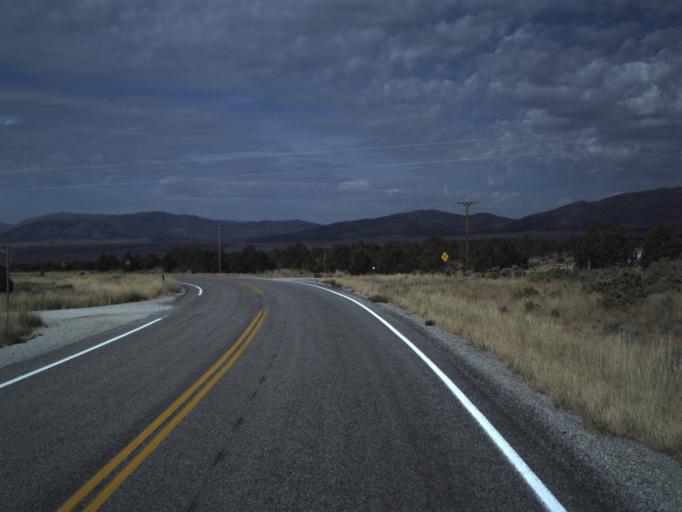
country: US
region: Idaho
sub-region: Cassia County
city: Burley
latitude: 41.8203
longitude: -113.4269
